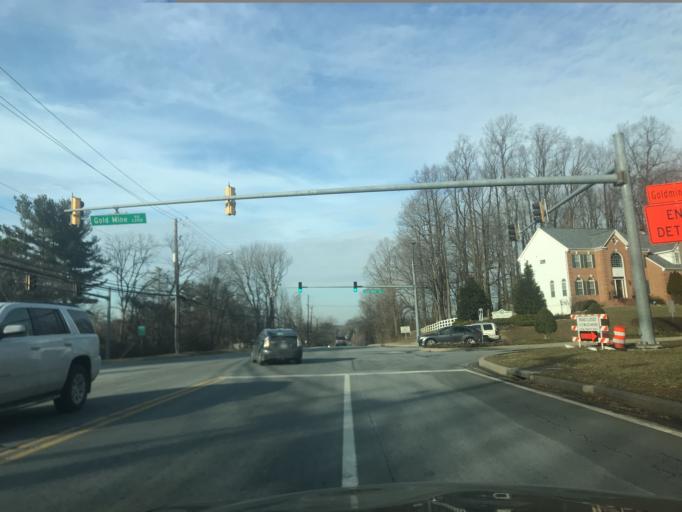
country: US
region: Maryland
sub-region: Montgomery County
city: Olney
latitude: 39.1716
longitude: -77.0592
